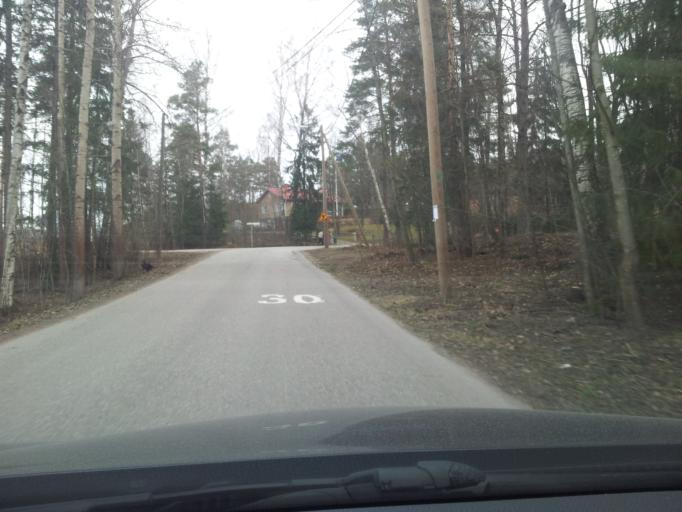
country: FI
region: Uusimaa
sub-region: Helsinki
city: Teekkarikylae
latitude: 60.2064
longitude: 24.8178
